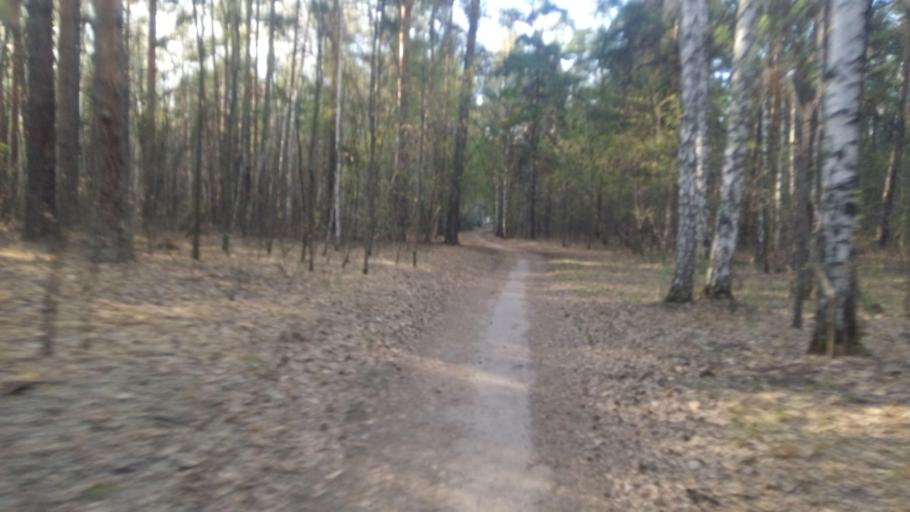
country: RU
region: Chelyabinsk
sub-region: Gorod Chelyabinsk
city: Chelyabinsk
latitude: 55.1490
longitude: 61.3368
